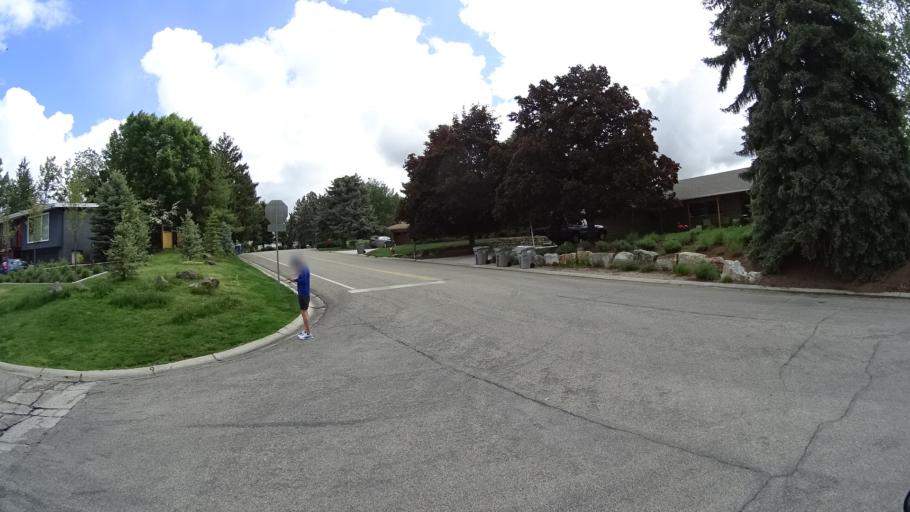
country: US
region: Idaho
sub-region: Ada County
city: Boise
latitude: 43.6453
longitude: -116.1841
